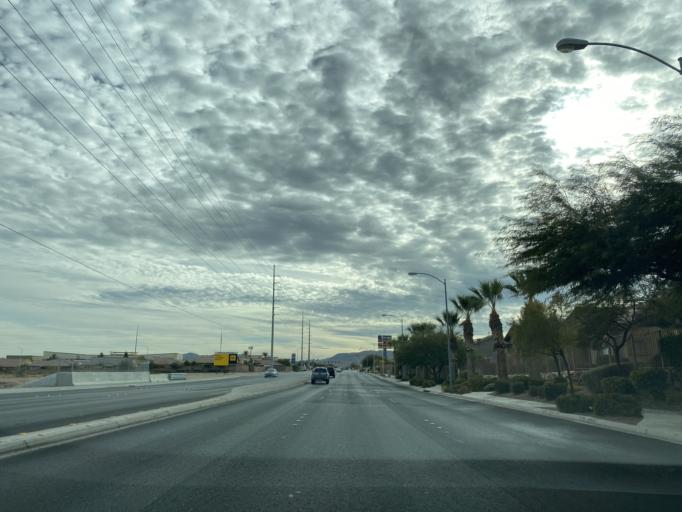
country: US
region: Nevada
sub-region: Clark County
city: Enterprise
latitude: 36.0246
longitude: -115.2789
